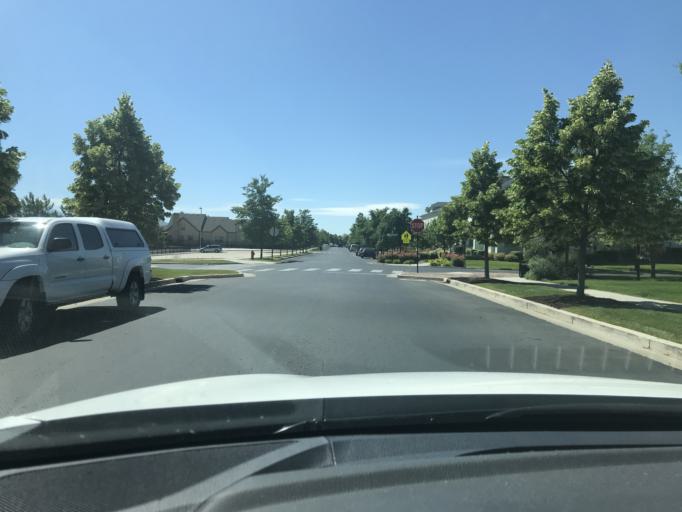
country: US
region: Utah
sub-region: Salt Lake County
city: South Jordan Heights
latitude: 40.5549
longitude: -111.9969
